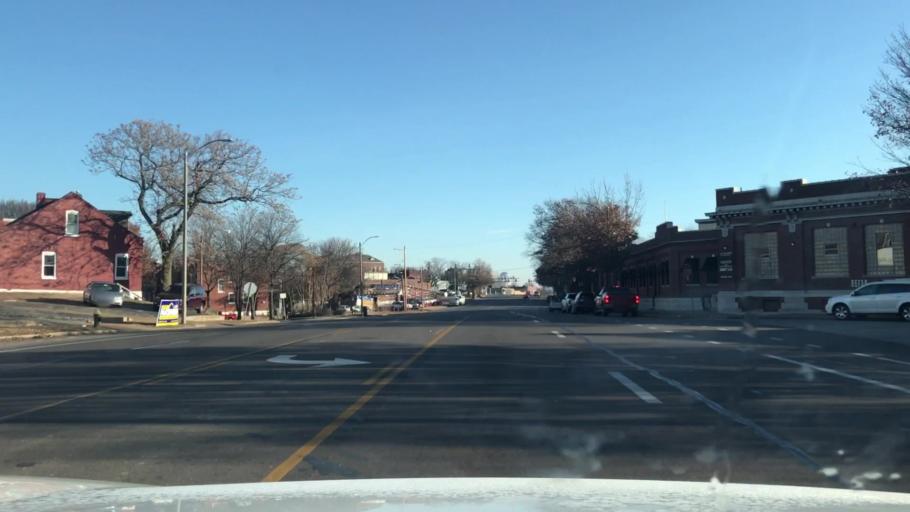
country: US
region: Missouri
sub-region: City of Saint Louis
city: St. Louis
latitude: 38.5990
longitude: -90.2351
